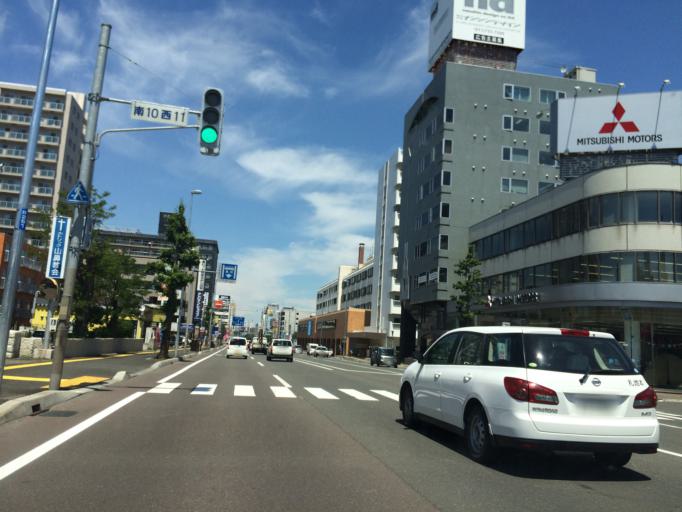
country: JP
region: Hokkaido
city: Sapporo
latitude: 43.0462
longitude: 141.3428
